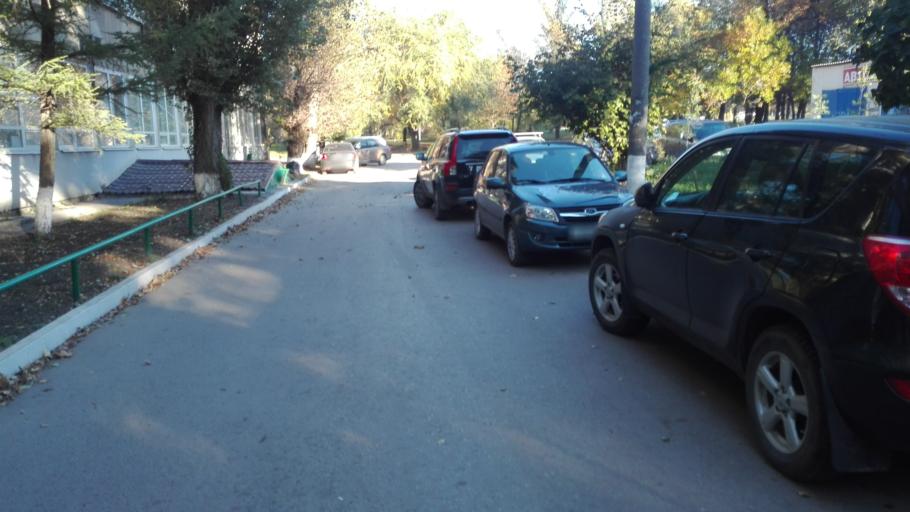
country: RU
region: Rostov
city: Rostov-na-Donu
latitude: 47.2137
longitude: 39.6289
